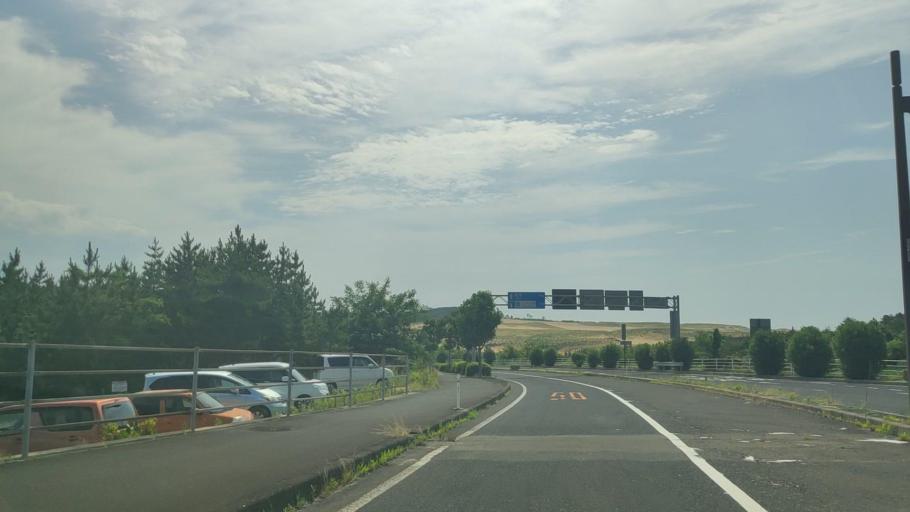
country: JP
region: Tottori
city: Tottori
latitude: 35.5386
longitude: 134.2376
